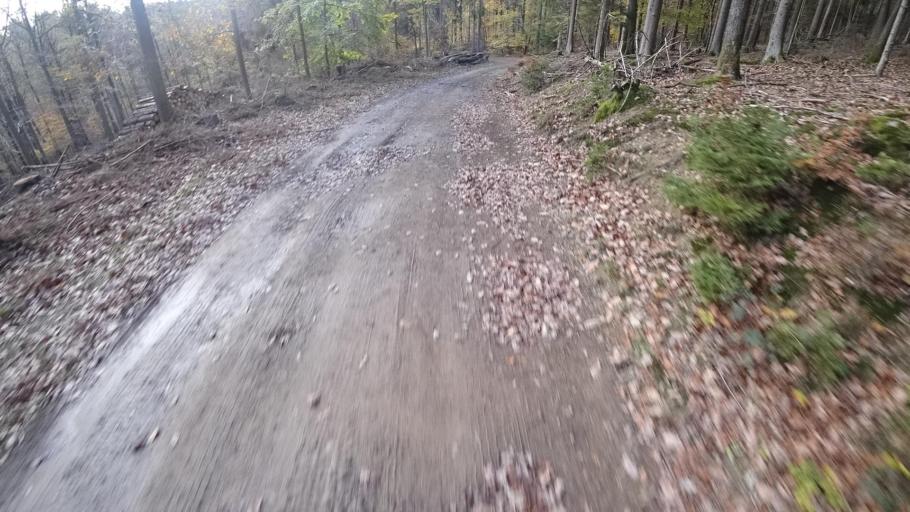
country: DE
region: Rheinland-Pfalz
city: Honningen
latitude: 50.4839
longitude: 6.9475
